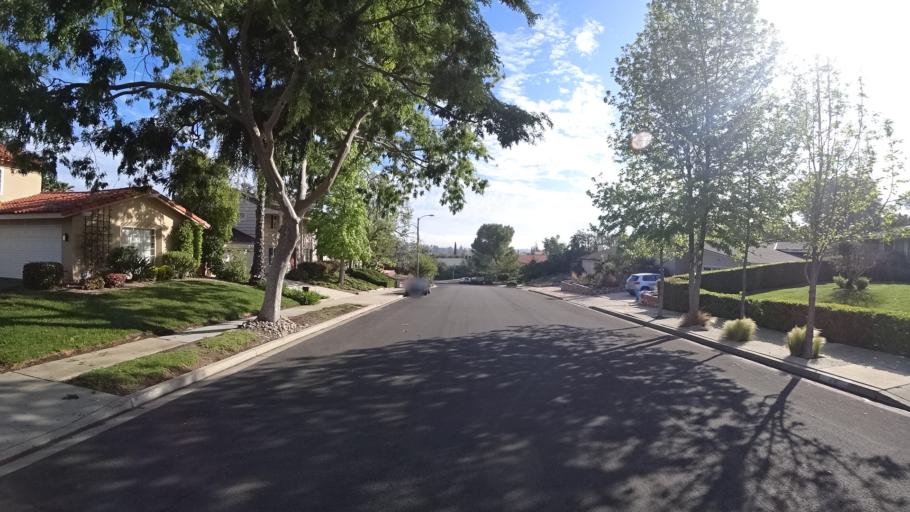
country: US
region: California
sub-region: Ventura County
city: Casa Conejo
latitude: 34.1785
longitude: -118.9481
